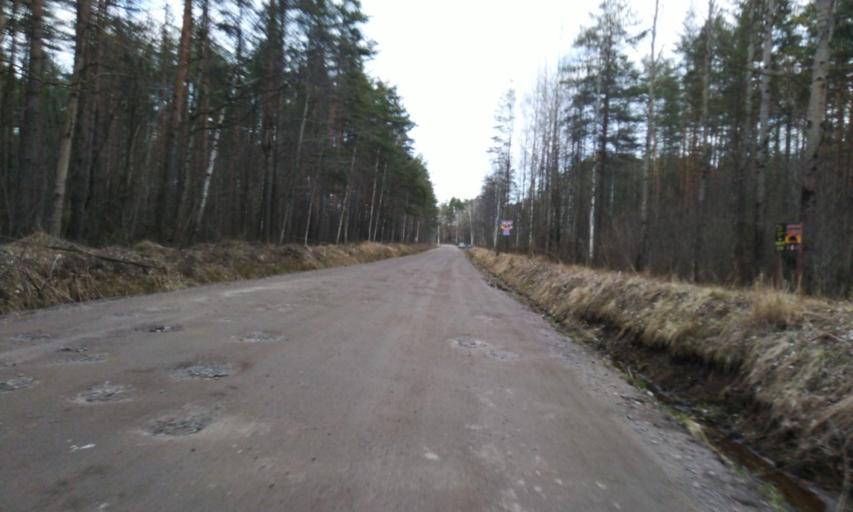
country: RU
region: Leningrad
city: Toksovo
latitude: 60.1168
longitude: 30.4815
